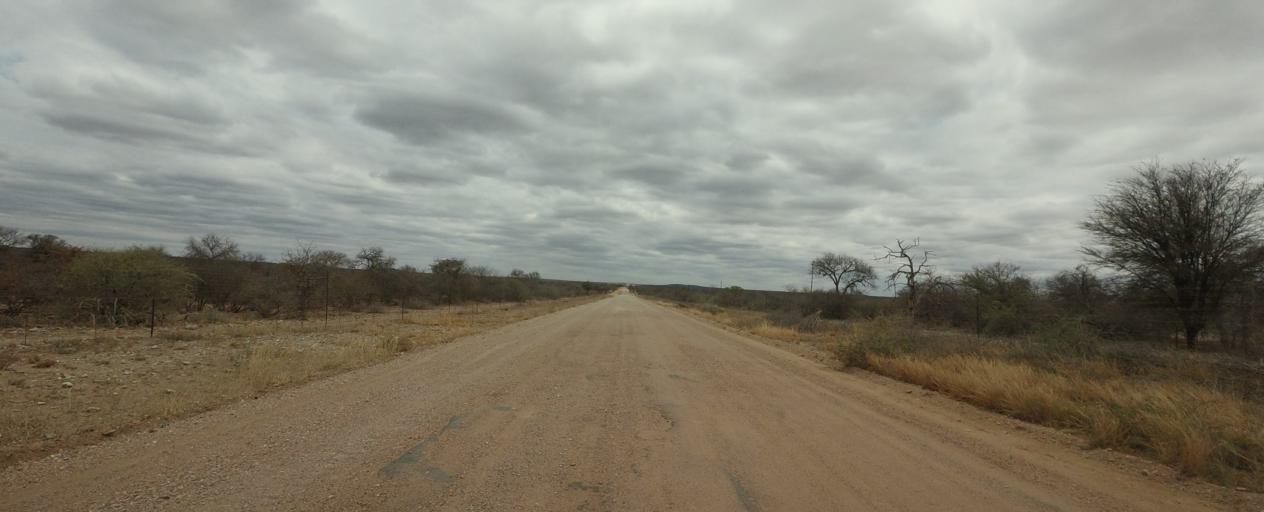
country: BW
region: Central
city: Mathathane
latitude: -22.7054
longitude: 28.5996
